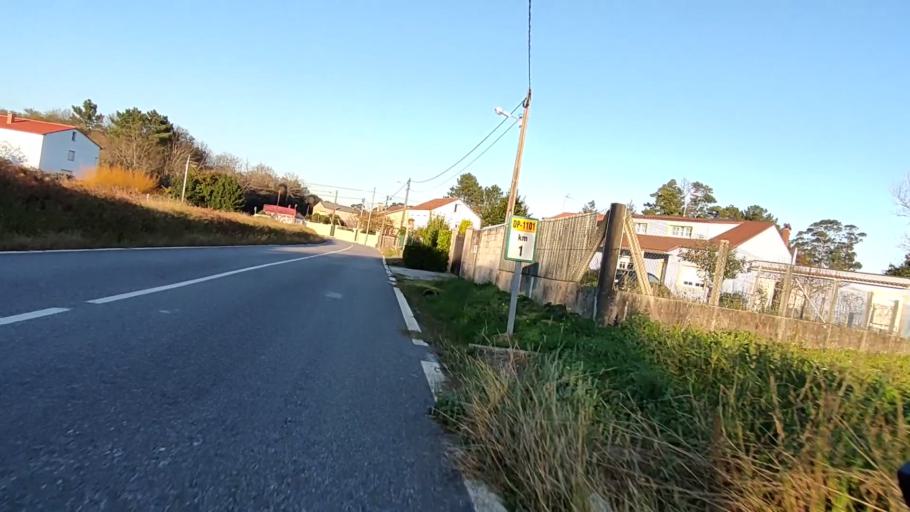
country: ES
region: Galicia
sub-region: Provincia da Coruna
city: Rianxo
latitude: 42.6359
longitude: -8.8565
